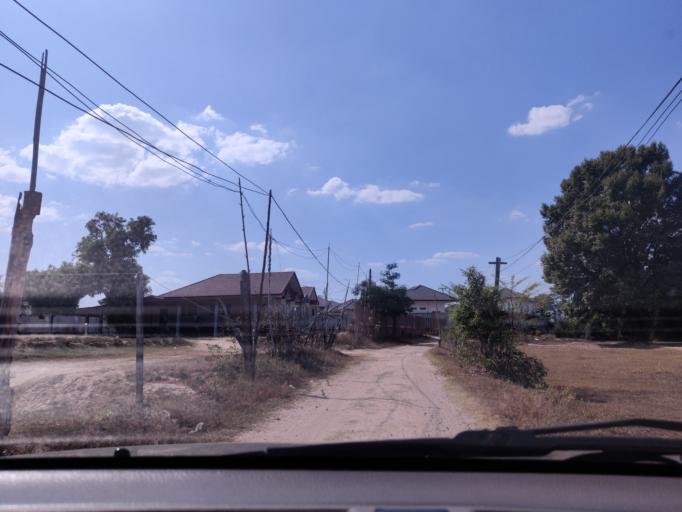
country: TH
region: Sisaket
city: Si Sa Ket
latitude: 15.1011
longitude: 104.3580
